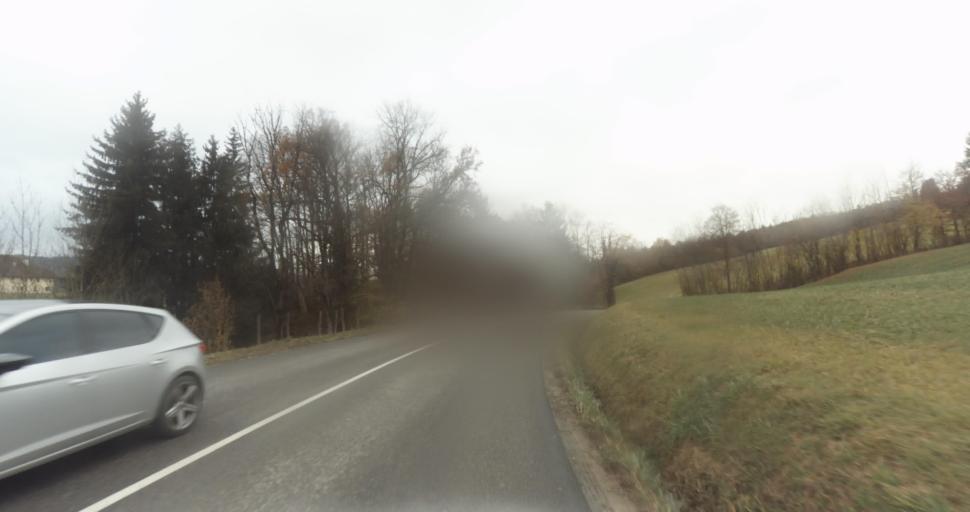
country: FR
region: Rhone-Alpes
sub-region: Departement de la Haute-Savoie
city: Thorens-Glieres
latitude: 45.9973
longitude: 6.2368
